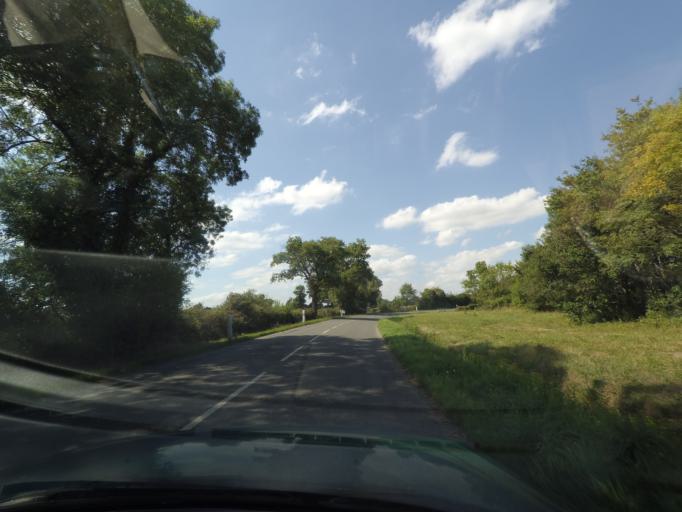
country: FR
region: Pays de la Loire
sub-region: Departement de la Loire-Atlantique
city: Sainte-Pazanne
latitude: 47.0792
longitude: -1.8051
